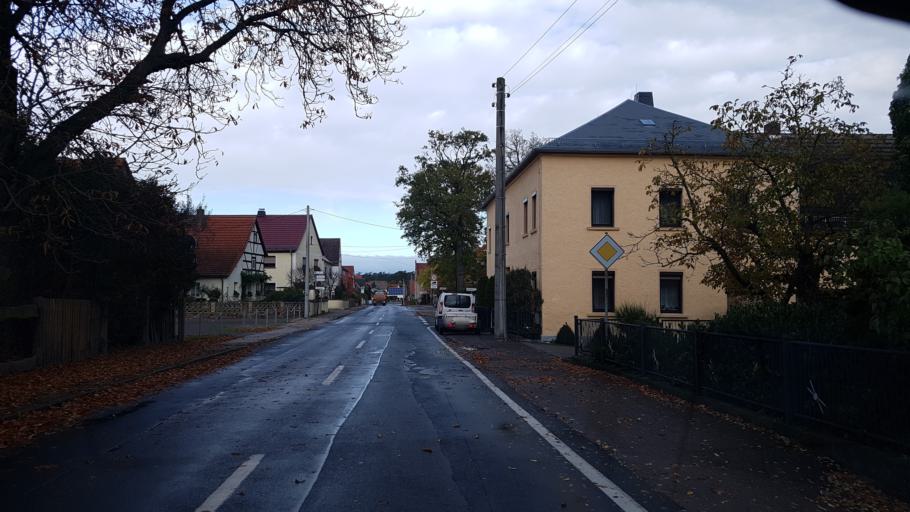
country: DE
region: Saxony
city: Dahlen
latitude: 51.3966
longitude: 12.9843
